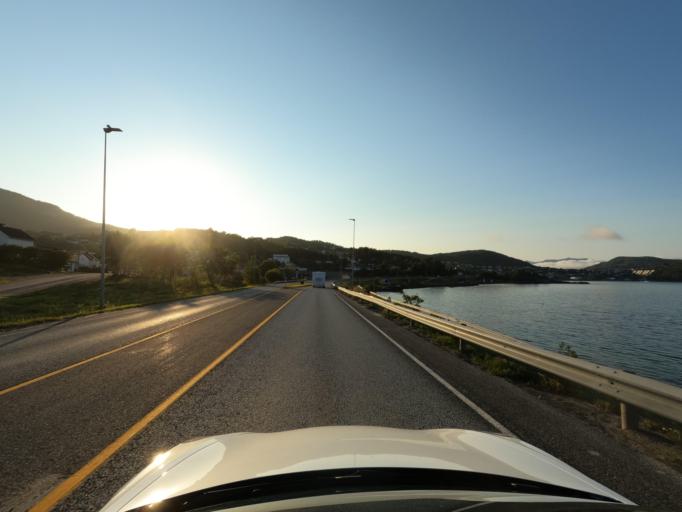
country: NO
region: Troms
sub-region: Harstad
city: Harstad
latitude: 68.7614
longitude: 16.5633
